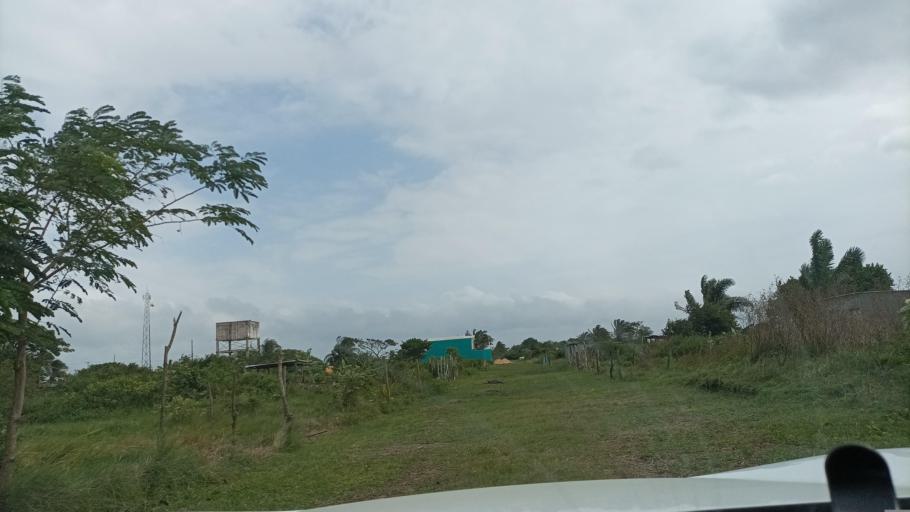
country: MX
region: Veracruz
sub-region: Coatzacoalcos
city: Fraccionamiento Ciudad Olmeca
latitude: 18.1787
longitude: -94.5945
